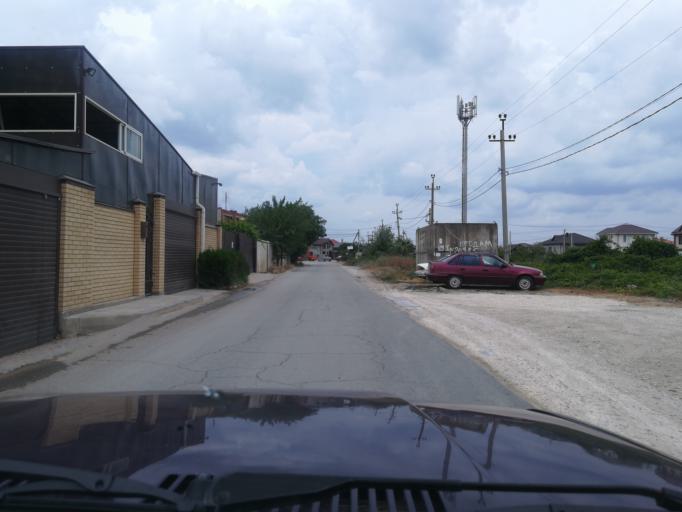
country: RU
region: Krasnodarskiy
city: Vityazevo
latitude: 45.0158
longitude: 37.2963
